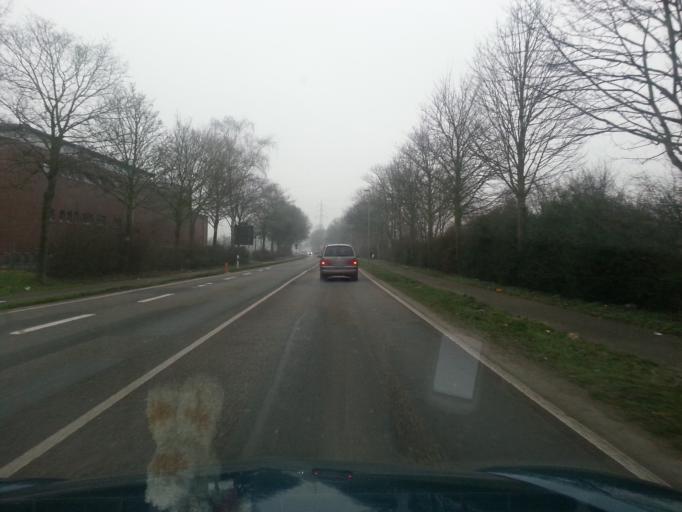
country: DE
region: North Rhine-Westphalia
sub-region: Regierungsbezirk Dusseldorf
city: Kleve
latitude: 51.7940
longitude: 6.1507
